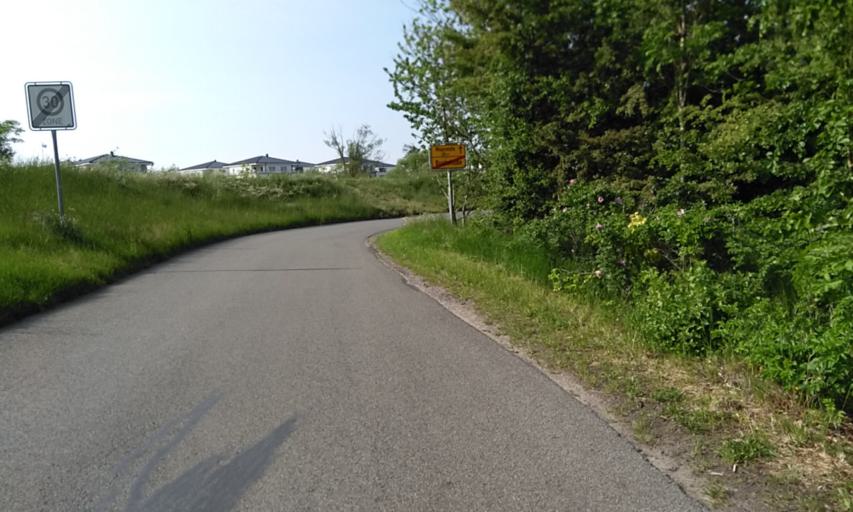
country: DE
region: Lower Saxony
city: Buxtehude
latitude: 53.4801
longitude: 9.7054
